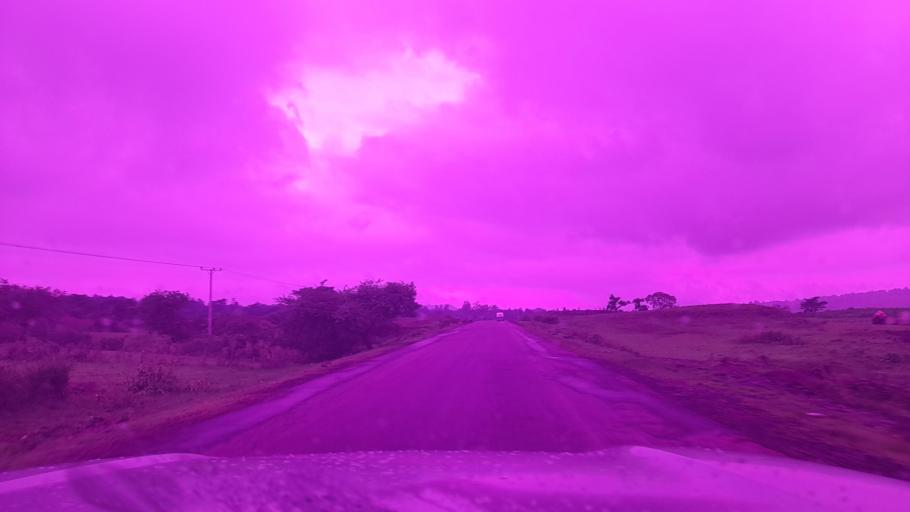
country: ET
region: Oromiya
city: Jima
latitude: 7.7777
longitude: 37.3419
